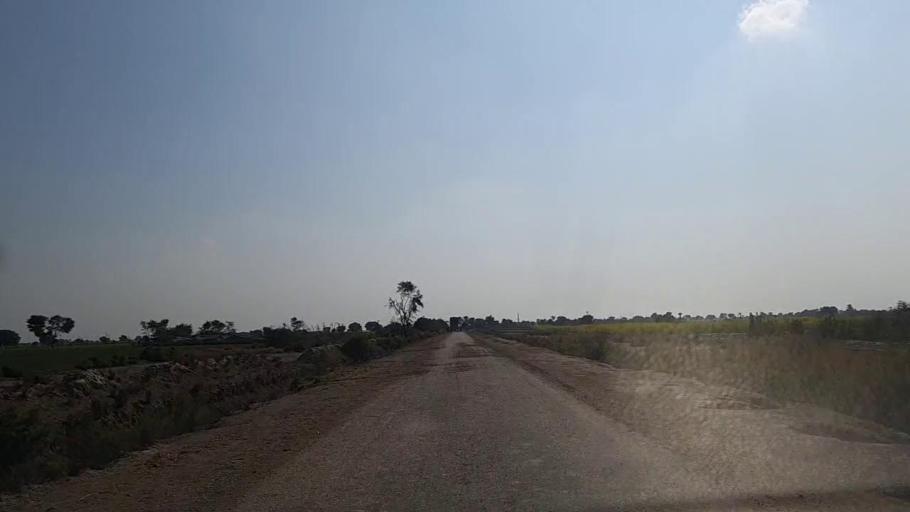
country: PK
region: Sindh
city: Jam Sahib
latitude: 26.2476
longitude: 68.5668
